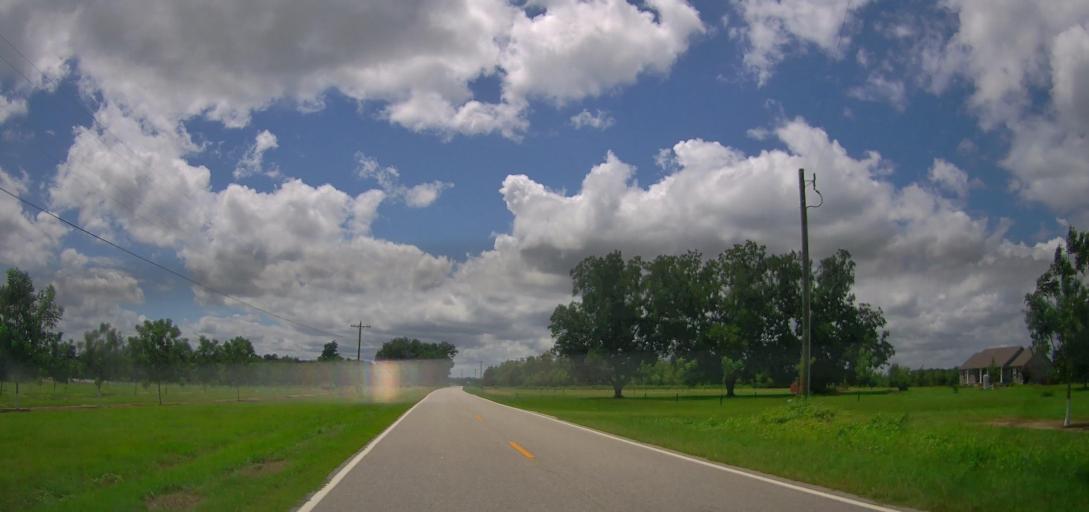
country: US
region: Georgia
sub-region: Irwin County
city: Ocilla
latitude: 31.6438
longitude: -83.2598
